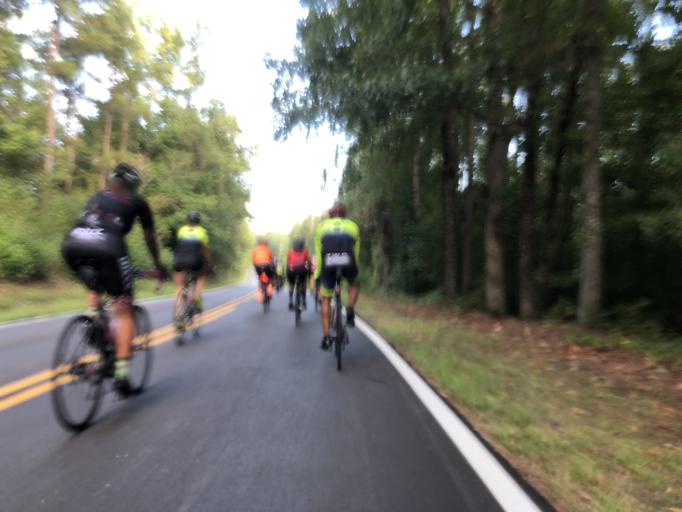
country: US
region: Georgia
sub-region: Fulton County
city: Palmetto
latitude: 33.5794
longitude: -84.6813
